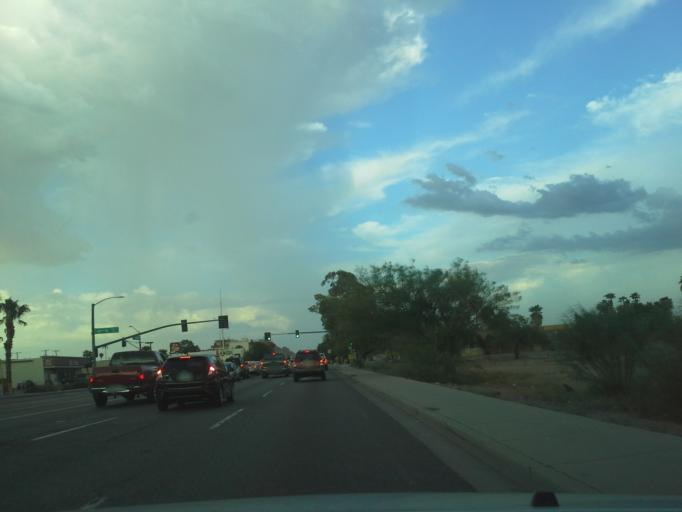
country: US
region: Arizona
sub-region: Maricopa County
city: Tempe Junction
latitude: 33.4656
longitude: -111.9967
